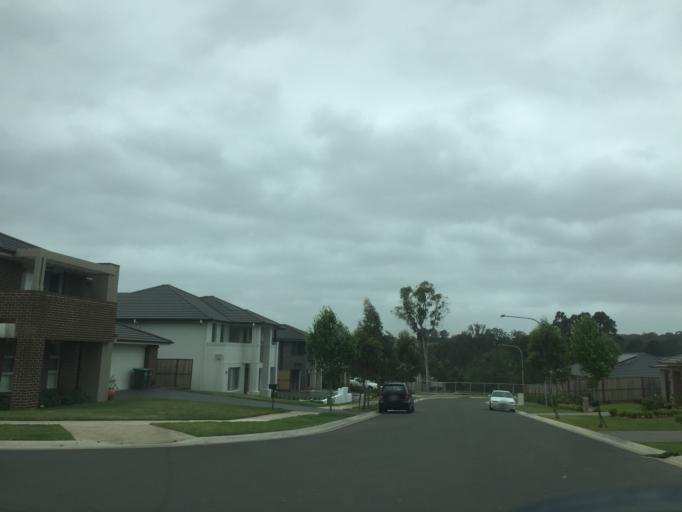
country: AU
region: New South Wales
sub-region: The Hills Shire
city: Beaumont Hills
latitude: -33.7224
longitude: 150.9536
